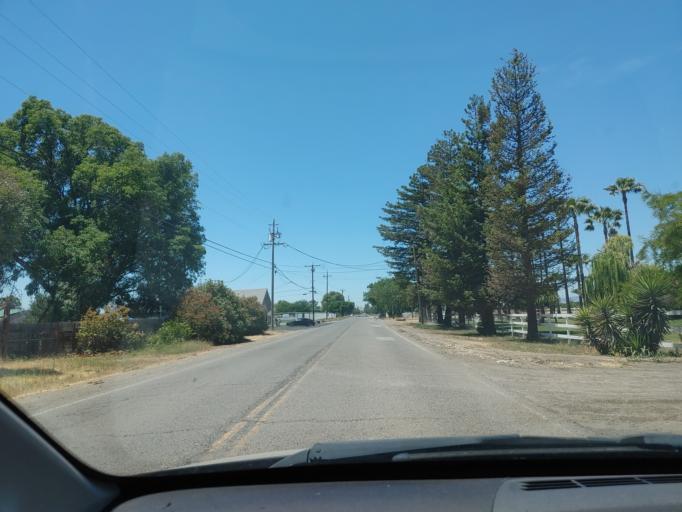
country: US
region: California
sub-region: San Benito County
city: Hollister
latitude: 36.8683
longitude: -121.3748
